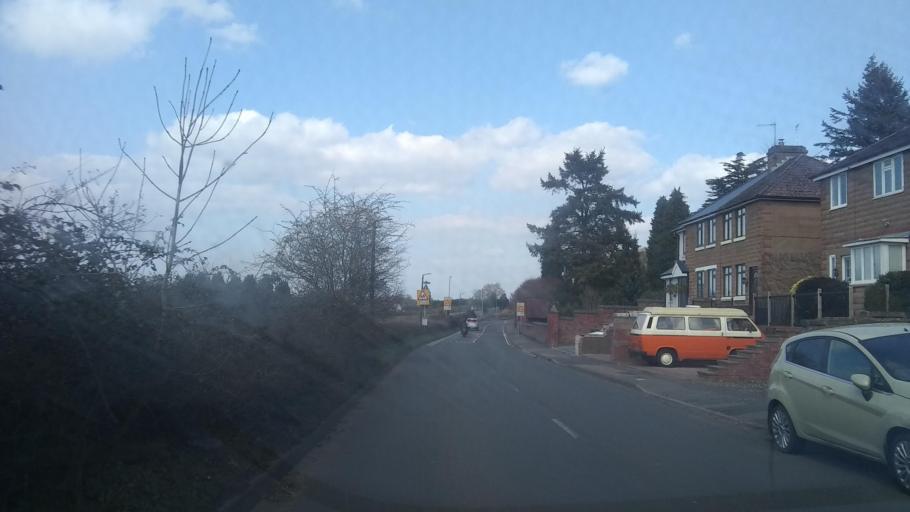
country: GB
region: England
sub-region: Worcestershire
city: Stourport-on-Severn
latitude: 52.3463
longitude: -2.2605
